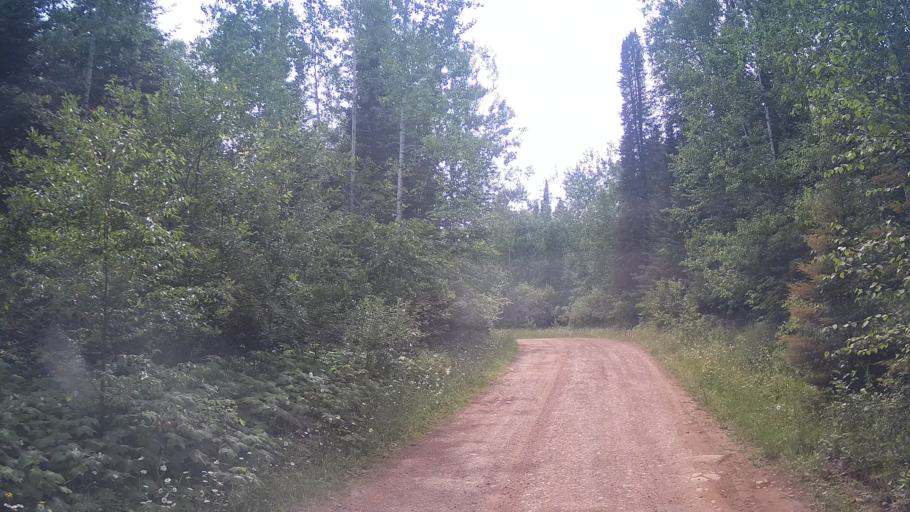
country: CA
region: Ontario
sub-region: Thunder Bay District
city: Thunder Bay
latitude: 48.6793
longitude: -88.6677
